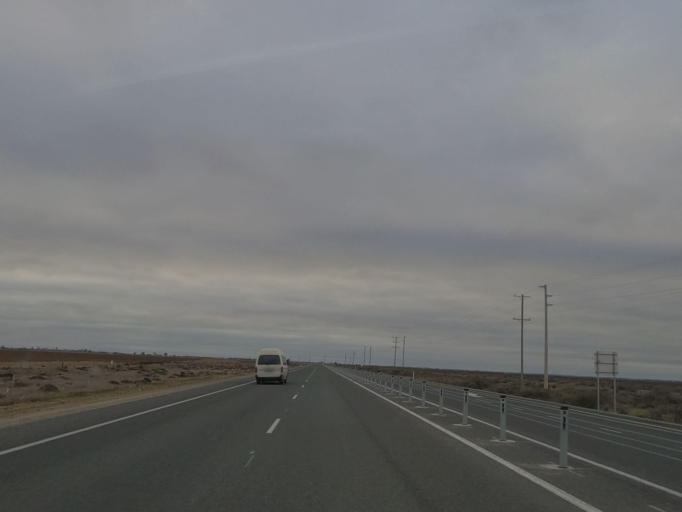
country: AU
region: Victoria
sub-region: Swan Hill
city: Swan Hill
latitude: -35.5153
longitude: 143.7275
